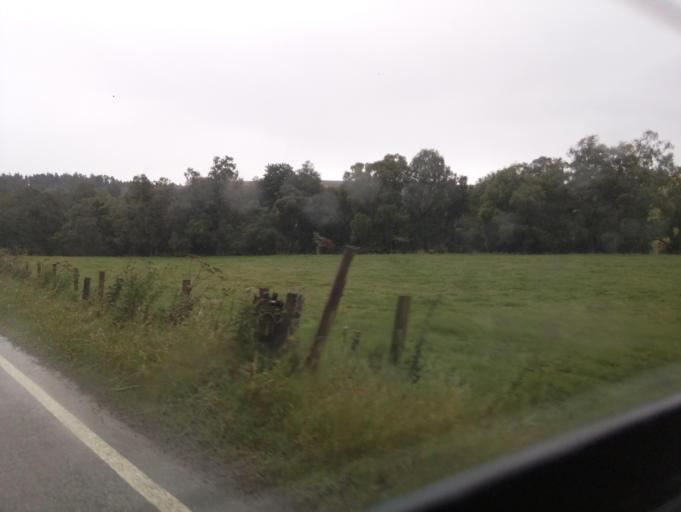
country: GB
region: Scotland
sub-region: Highland
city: Grantown on Spey
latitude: 57.2589
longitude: -3.4098
